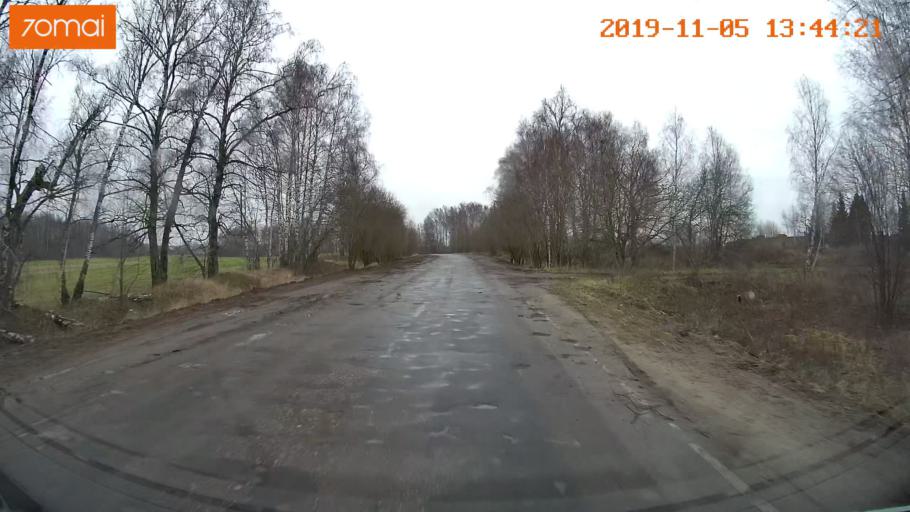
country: RU
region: Ivanovo
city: Shuya
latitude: 56.9810
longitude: 41.4102
